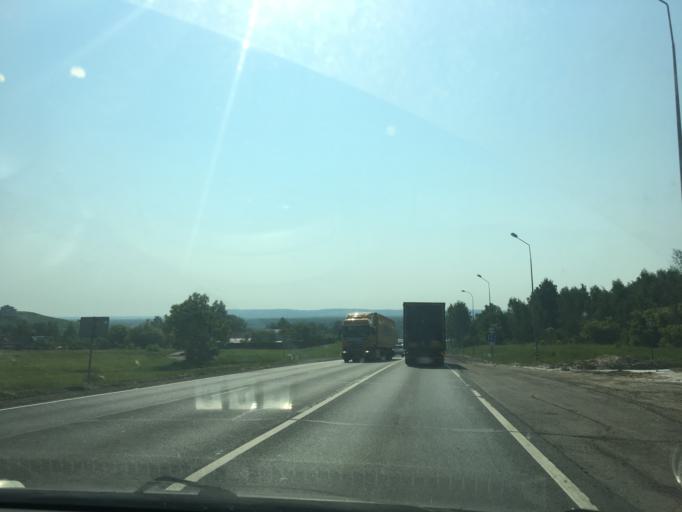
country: RU
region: Nizjnij Novgorod
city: Kstovo
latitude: 56.1030
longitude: 44.2973
